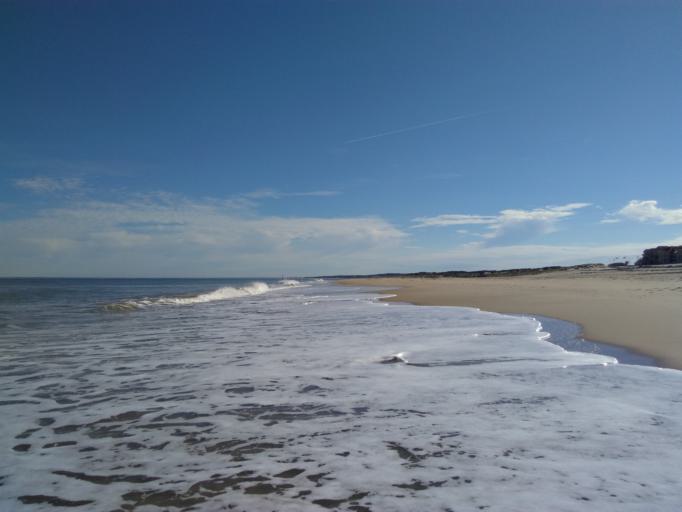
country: FR
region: Aquitaine
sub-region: Departement de la Gironde
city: Soulac-sur-Mer
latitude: 45.5161
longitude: -1.1301
